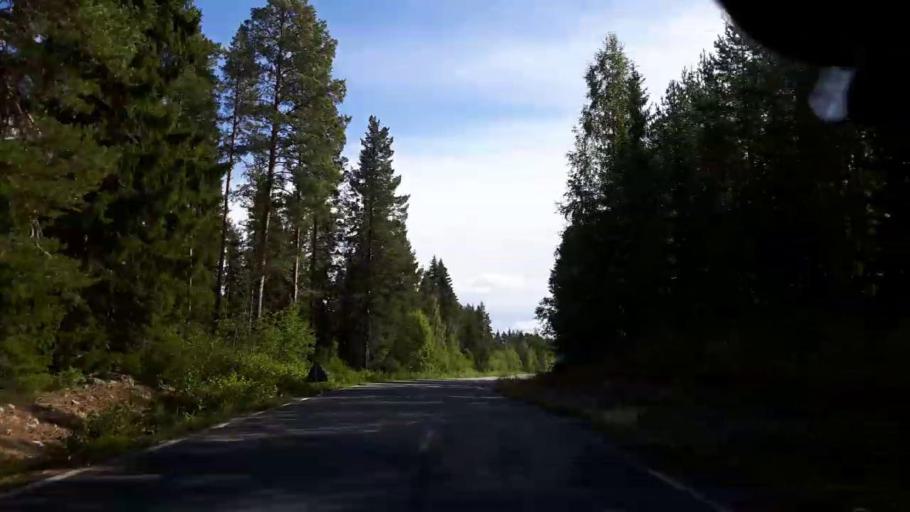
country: SE
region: Jaemtland
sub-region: Braecke Kommun
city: Braecke
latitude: 63.2039
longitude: 15.3574
